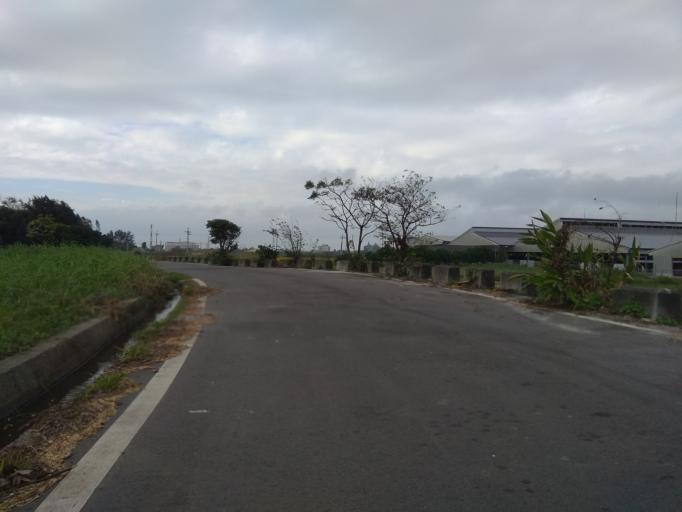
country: TW
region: Taiwan
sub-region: Hsinchu
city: Zhubei
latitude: 24.9779
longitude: 121.0373
